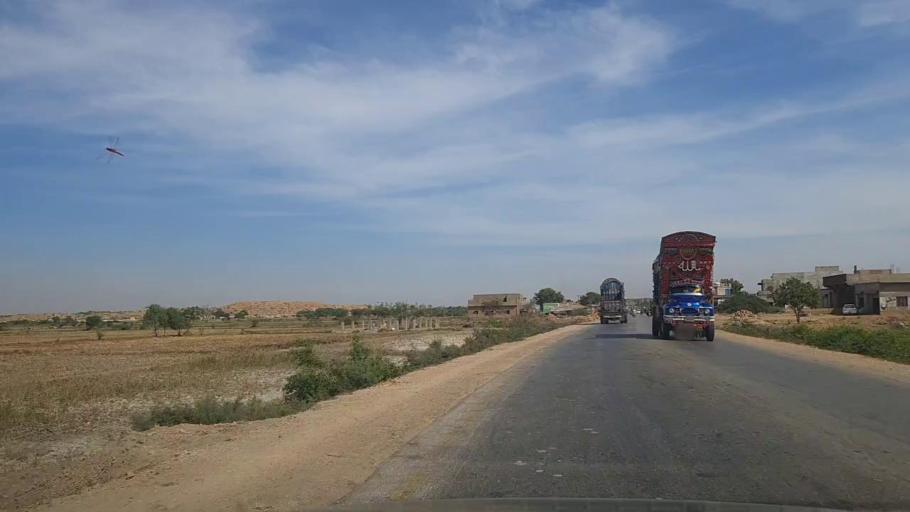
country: PK
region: Sindh
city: Daro Mehar
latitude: 24.9812
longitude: 68.1316
